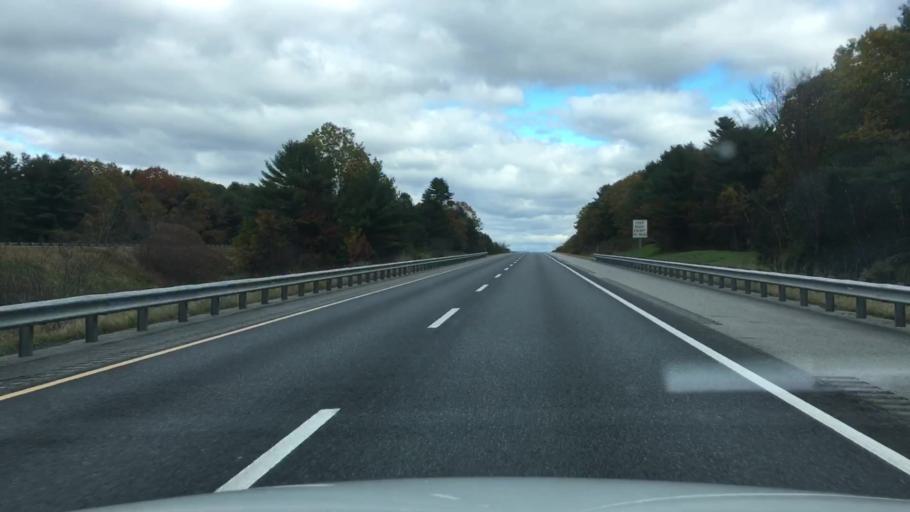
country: US
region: Maine
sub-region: Sagadahoc County
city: Richmond
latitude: 44.0352
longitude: -69.9053
